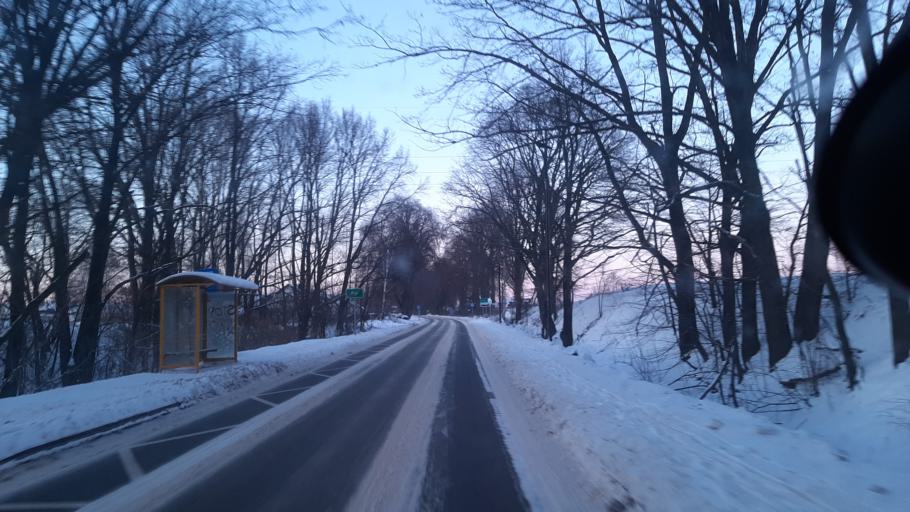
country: PL
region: Lublin Voivodeship
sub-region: Powiat lubelski
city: Lublin
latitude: 51.3207
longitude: 22.5611
